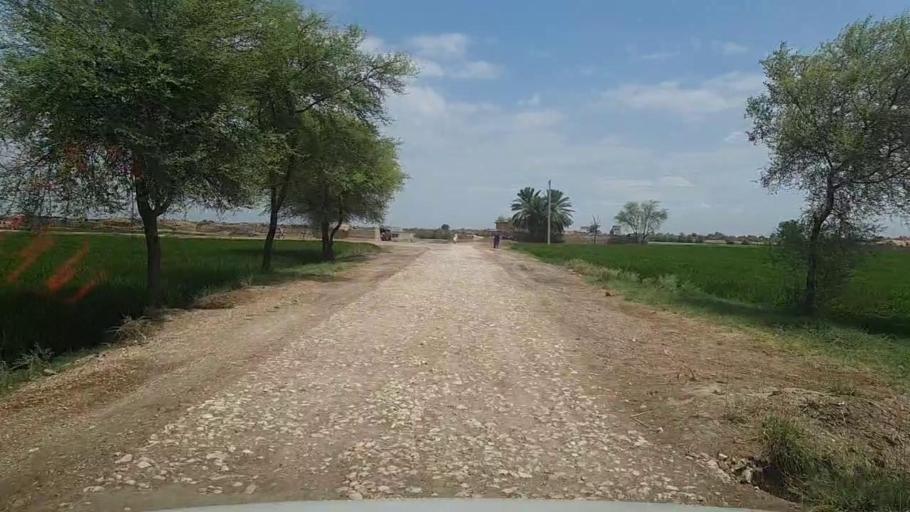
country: PK
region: Sindh
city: Kandhkot
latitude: 28.3420
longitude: 69.2211
